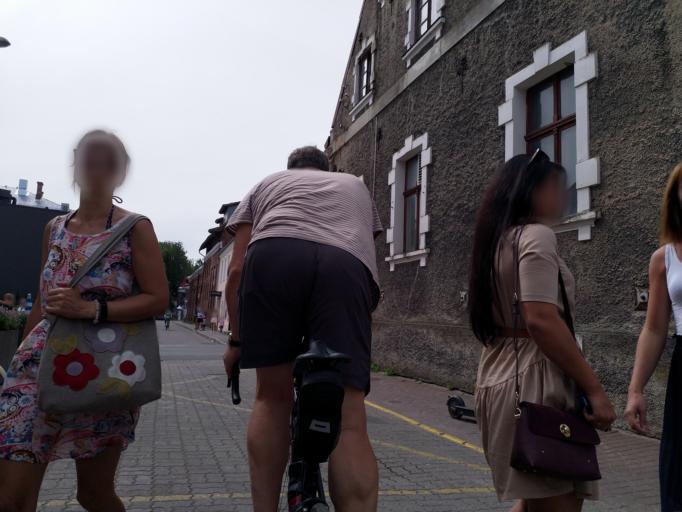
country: EE
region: Paernumaa
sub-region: Paernu linn
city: Parnu
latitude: 58.3841
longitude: 24.5013
